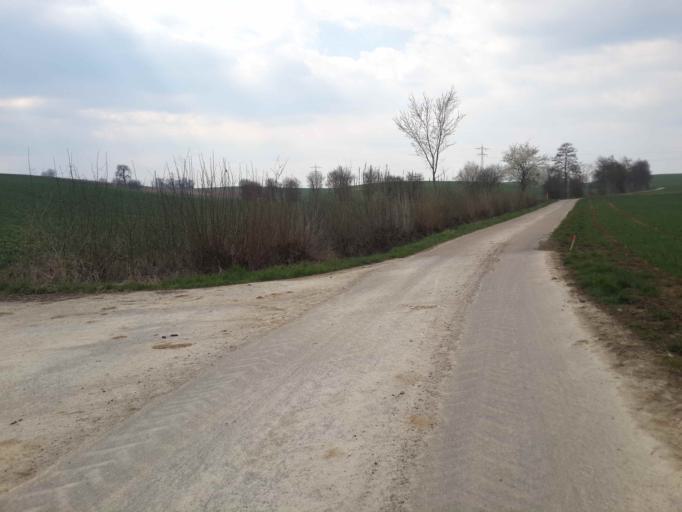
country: DE
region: Baden-Wuerttemberg
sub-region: Regierungsbezirk Stuttgart
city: Ittlingen
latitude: 49.1635
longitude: 8.9321
